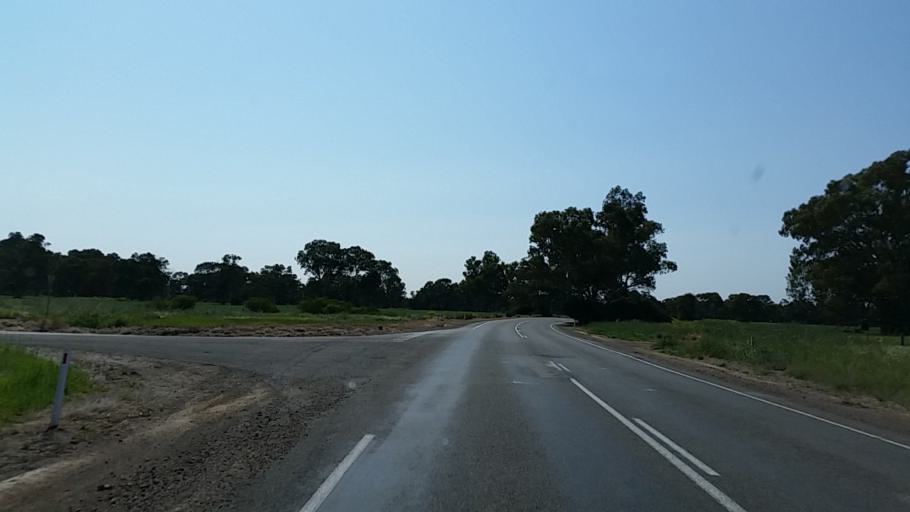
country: AU
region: South Australia
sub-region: Port Pirie City and Dists
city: Crystal Brook
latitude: -33.2646
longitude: 138.3324
